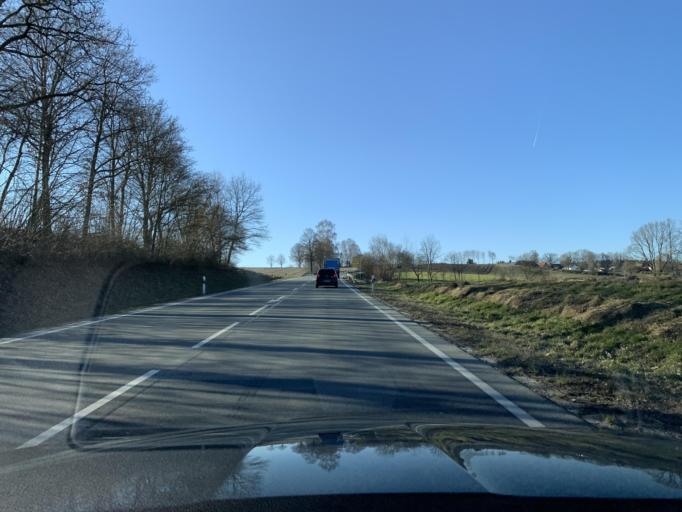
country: DE
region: Bavaria
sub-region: Upper Palatinate
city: Willmering
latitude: 49.2525
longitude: 12.6455
